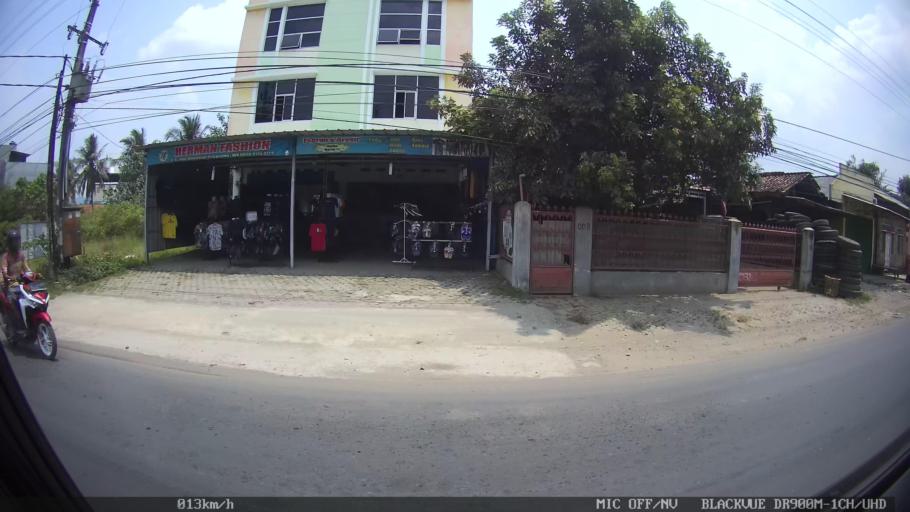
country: ID
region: Lampung
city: Pringsewu
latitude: -5.3583
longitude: 104.9892
